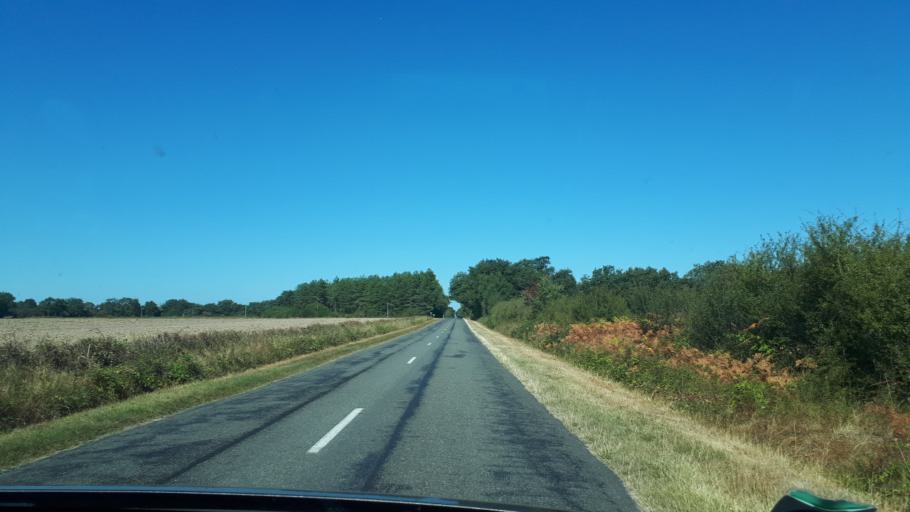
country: FR
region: Centre
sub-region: Departement du Loiret
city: Coullons
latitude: 47.6320
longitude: 2.4655
